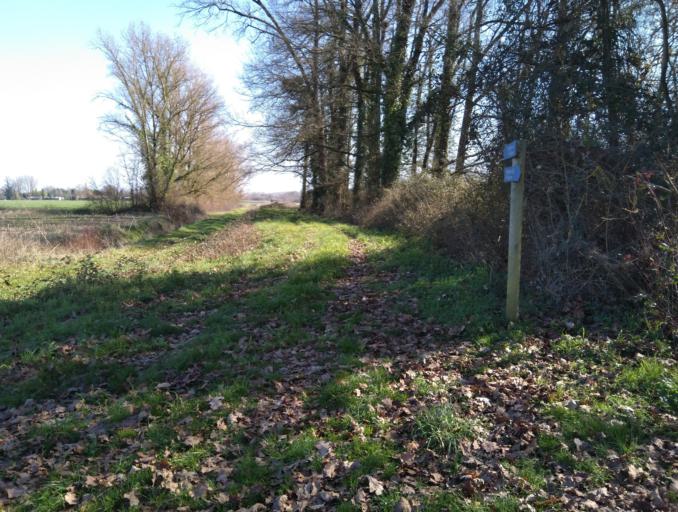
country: FR
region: Midi-Pyrenees
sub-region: Departement du Gers
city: Riscle
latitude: 43.6627
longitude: -0.1620
